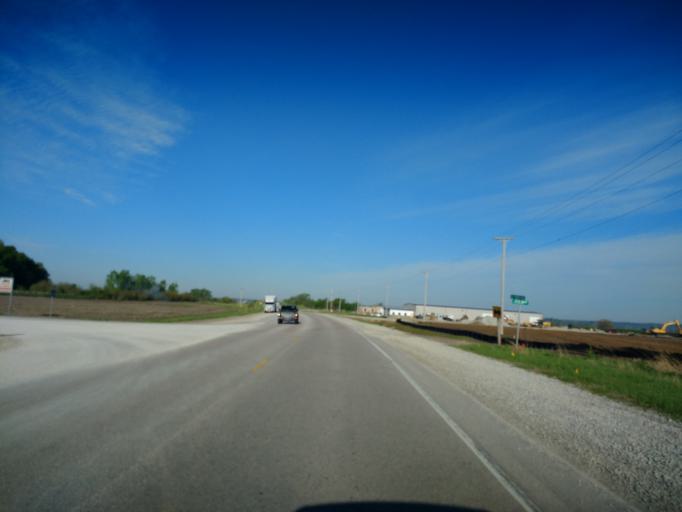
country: US
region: Iowa
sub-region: Pottawattamie County
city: Carter Lake
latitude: 41.3623
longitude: -95.8705
